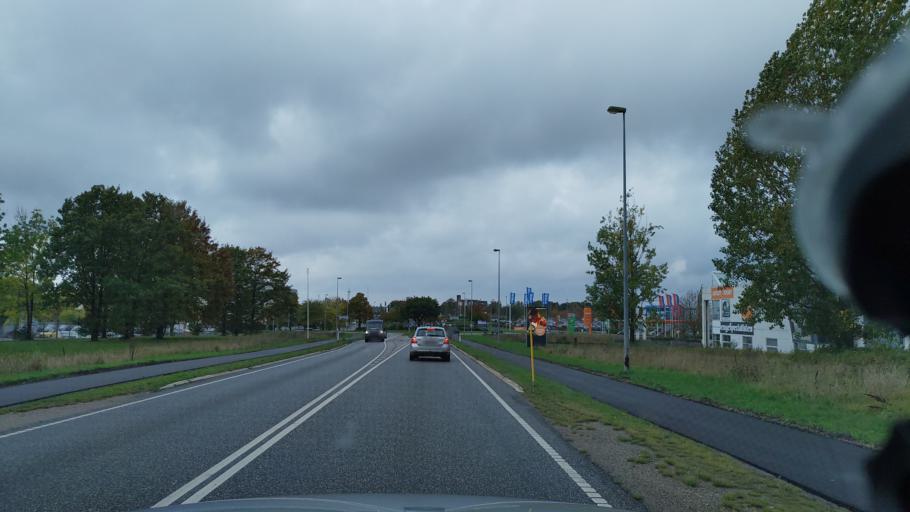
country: DK
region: Zealand
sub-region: Naestved Kommune
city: Fensmark
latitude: 55.2529
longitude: 11.7901
